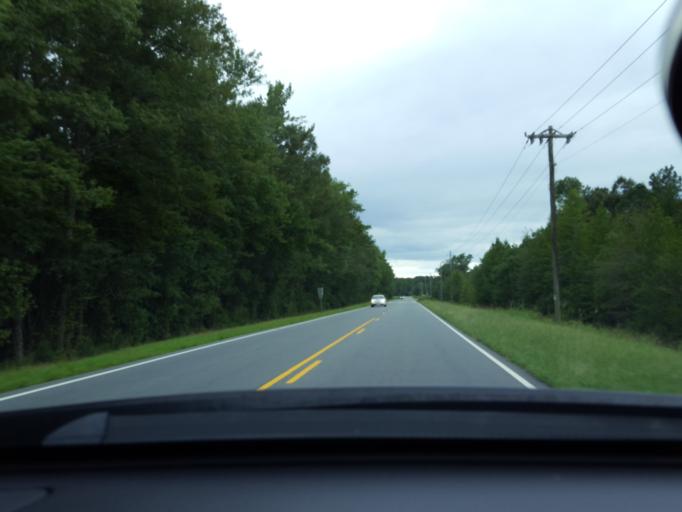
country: US
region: North Carolina
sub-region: Sampson County
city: Roseboro
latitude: 34.7604
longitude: -78.4104
